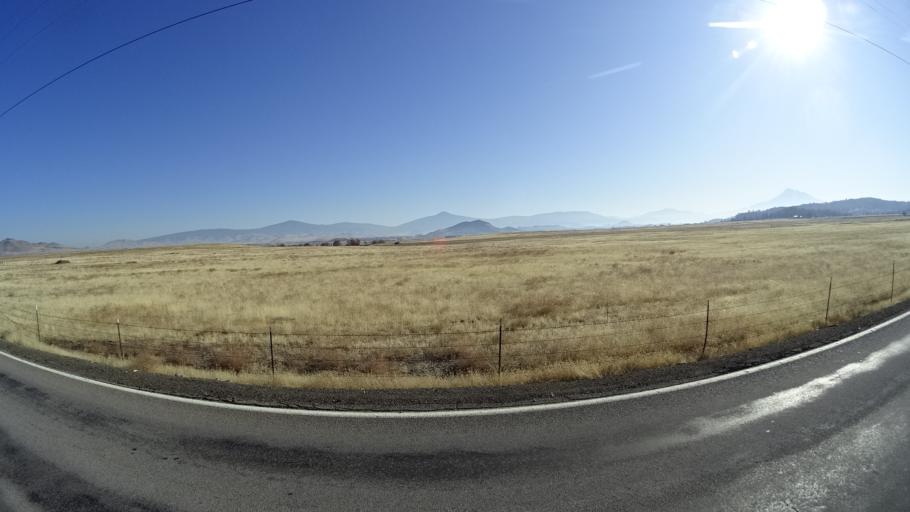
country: US
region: California
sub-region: Siskiyou County
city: Yreka
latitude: 41.7184
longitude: -122.5934
